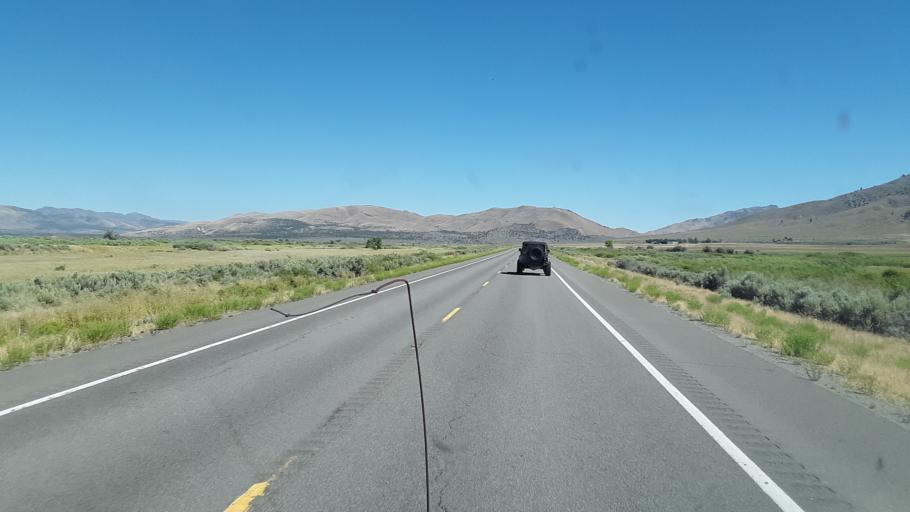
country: US
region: Nevada
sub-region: Washoe County
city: Cold Springs
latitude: 39.9728
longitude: -120.0588
